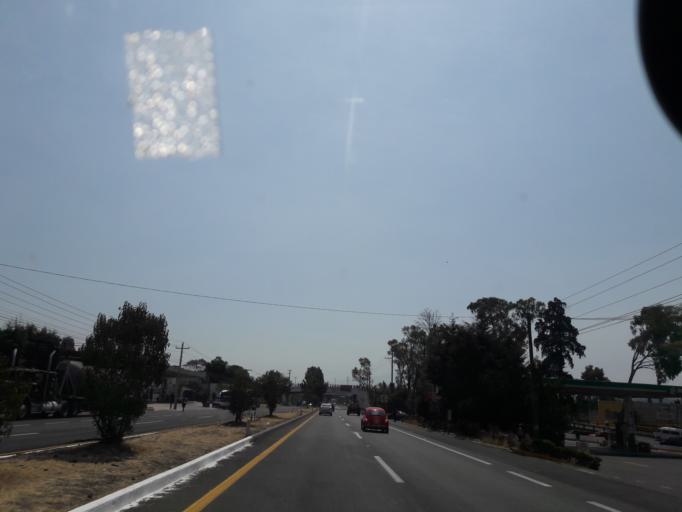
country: MX
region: Tlaxcala
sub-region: Totolac
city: Zaragoza
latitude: 19.3213
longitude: -98.2663
